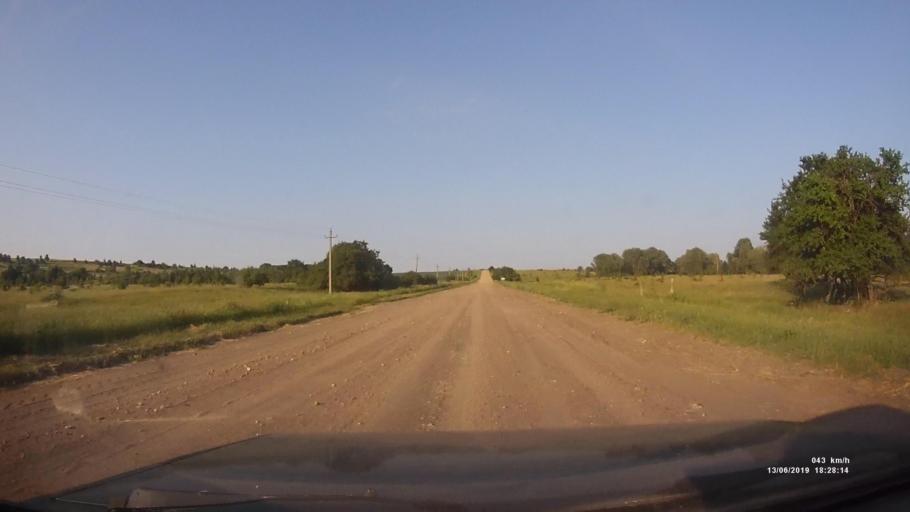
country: RU
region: Rostov
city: Kazanskaya
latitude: 49.8561
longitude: 41.3303
